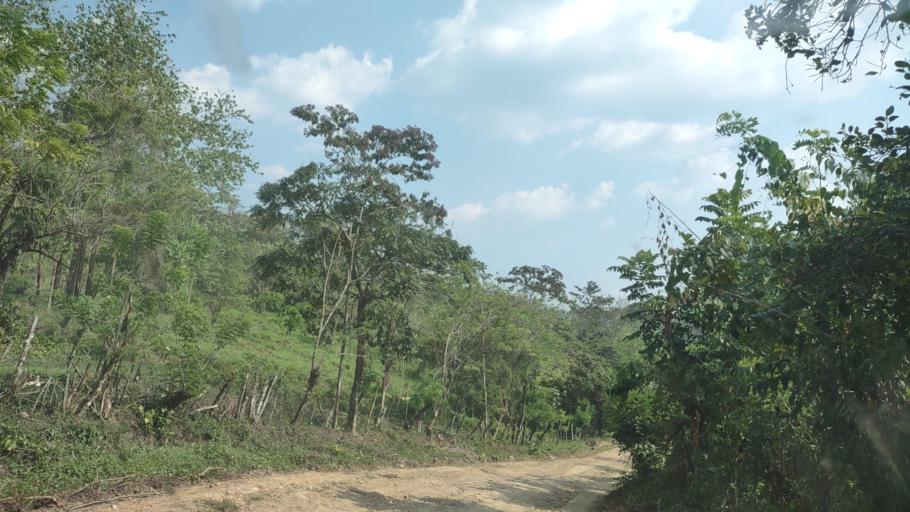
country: MX
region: Chiapas
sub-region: Tecpatan
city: Raudales Malpaso
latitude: 17.3298
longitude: -93.7471
